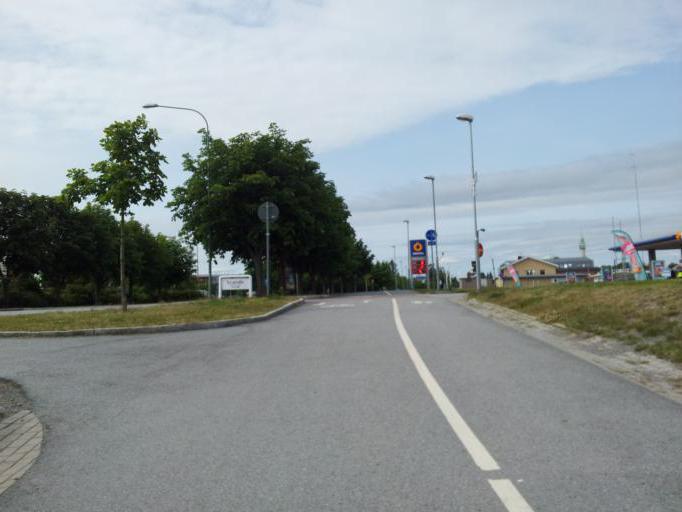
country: SE
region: Uppsala
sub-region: Uppsala Kommun
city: Uppsala
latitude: 59.8753
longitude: 17.6424
